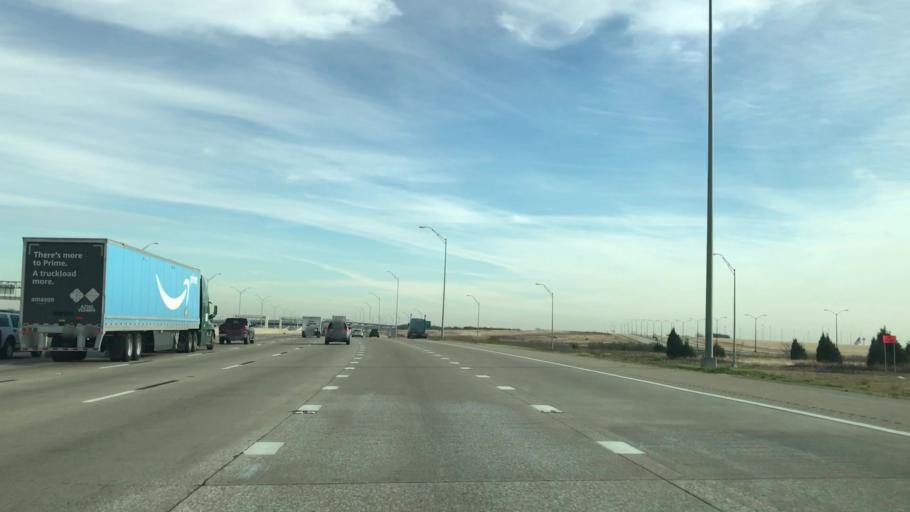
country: US
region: Texas
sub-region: Tarrant County
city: Grapevine
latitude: 32.9234
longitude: -97.0591
